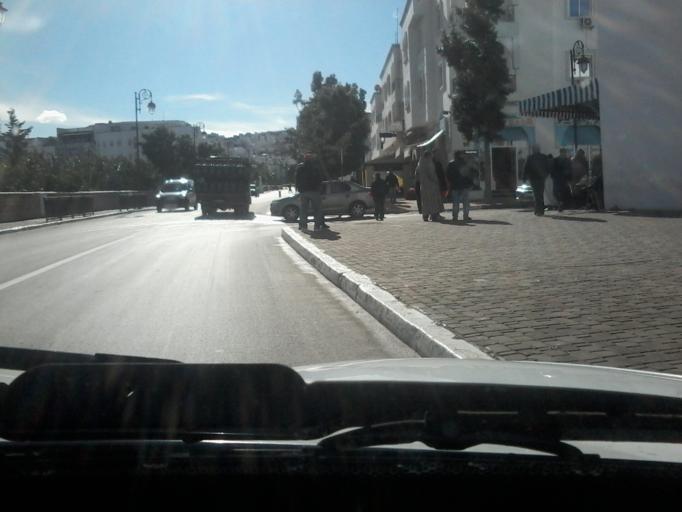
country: MA
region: Tanger-Tetouan
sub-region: Tetouan
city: Martil
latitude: 35.6891
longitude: -5.3301
